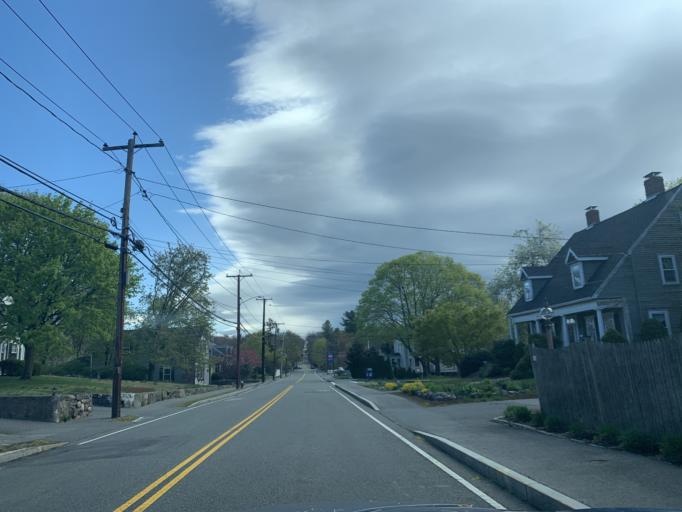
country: US
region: Massachusetts
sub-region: Norfolk County
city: Milton
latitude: 42.2437
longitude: -71.0964
